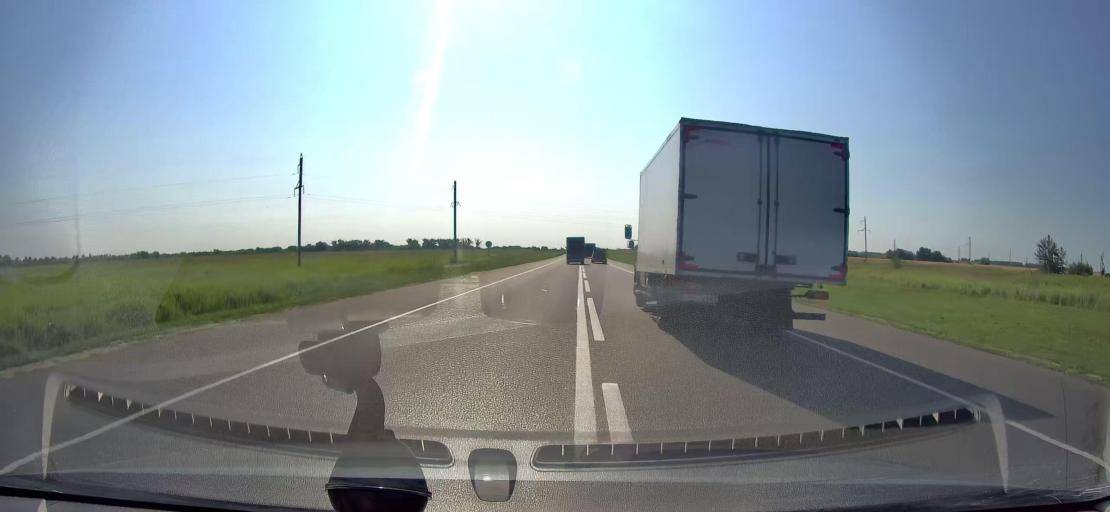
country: RU
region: Orjol
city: Kromy
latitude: 52.6523
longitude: 35.7285
